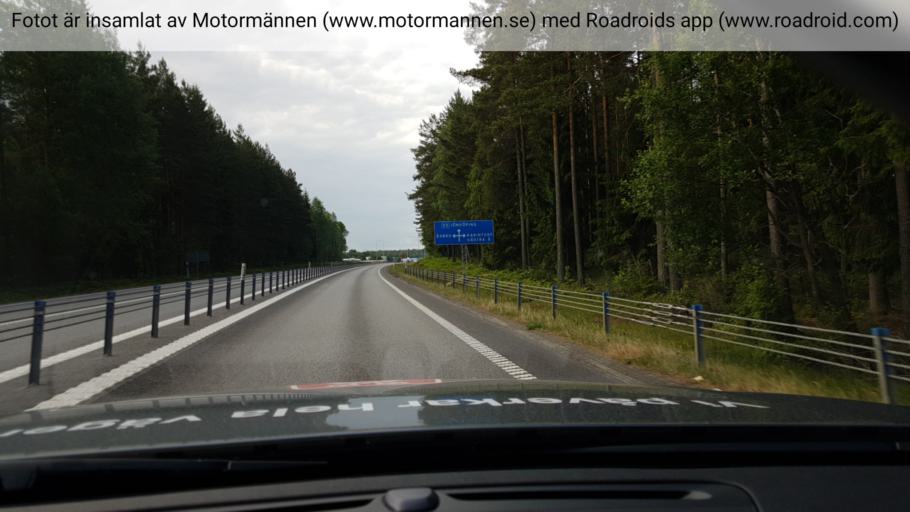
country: SE
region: OErebro
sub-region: Askersunds Kommun
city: Asbro
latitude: 59.0059
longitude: 15.0435
